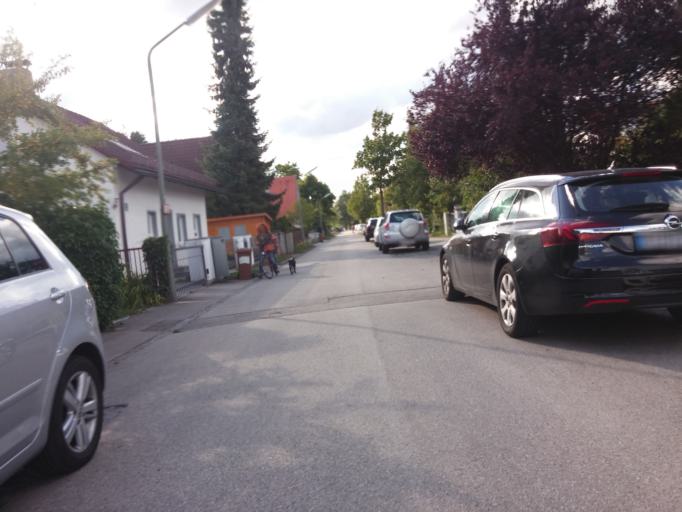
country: DE
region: Bavaria
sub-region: Upper Bavaria
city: Haar
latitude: 48.1201
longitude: 11.7006
